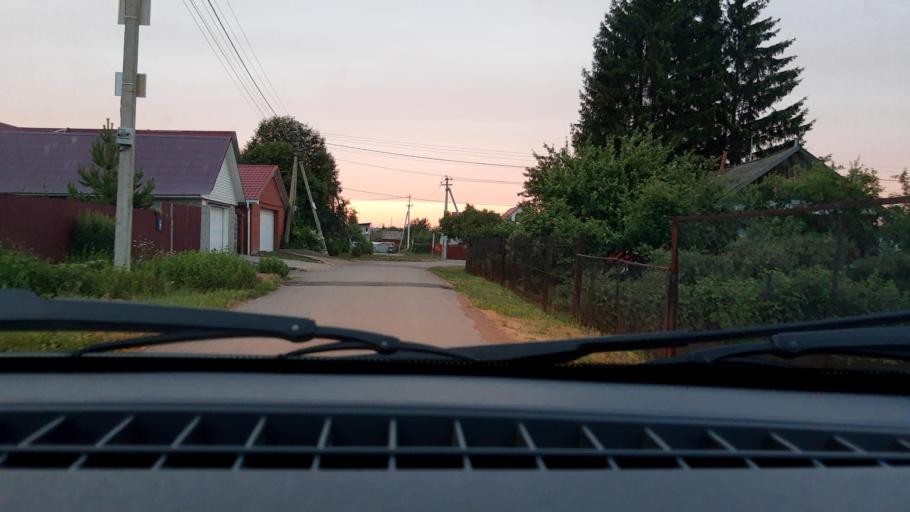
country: RU
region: Bashkortostan
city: Mikhaylovka
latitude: 54.8013
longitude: 55.7721
